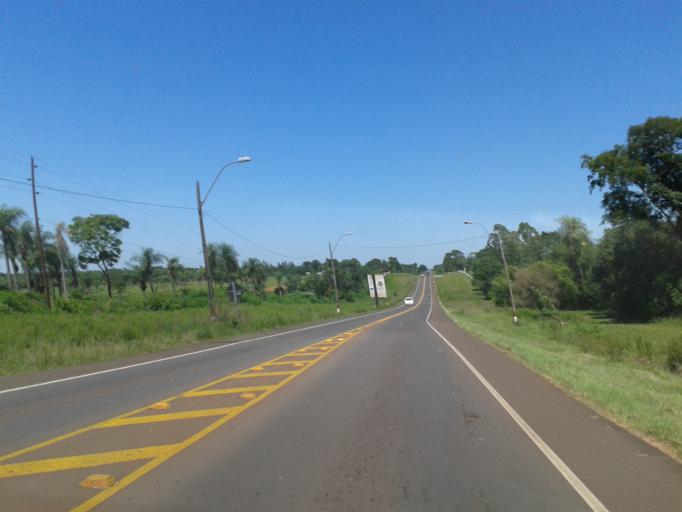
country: PY
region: Misiones
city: Santa Rosa
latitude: -26.8896
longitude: -56.8689
